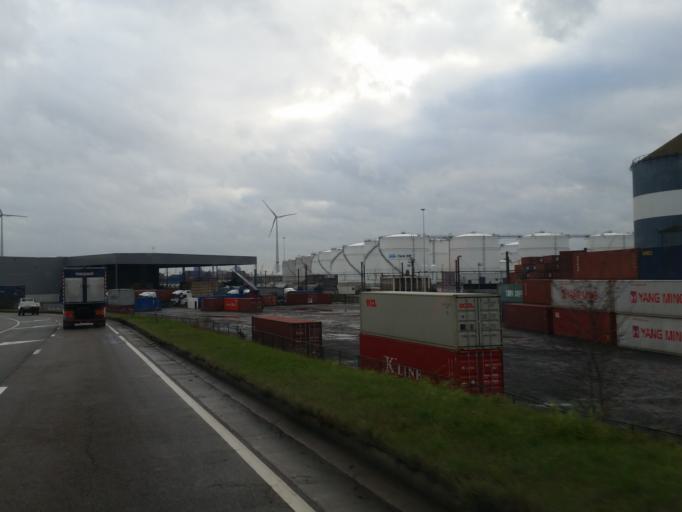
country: BE
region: Flanders
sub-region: Provincie Antwerpen
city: Stabroek
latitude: 51.2979
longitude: 4.3382
